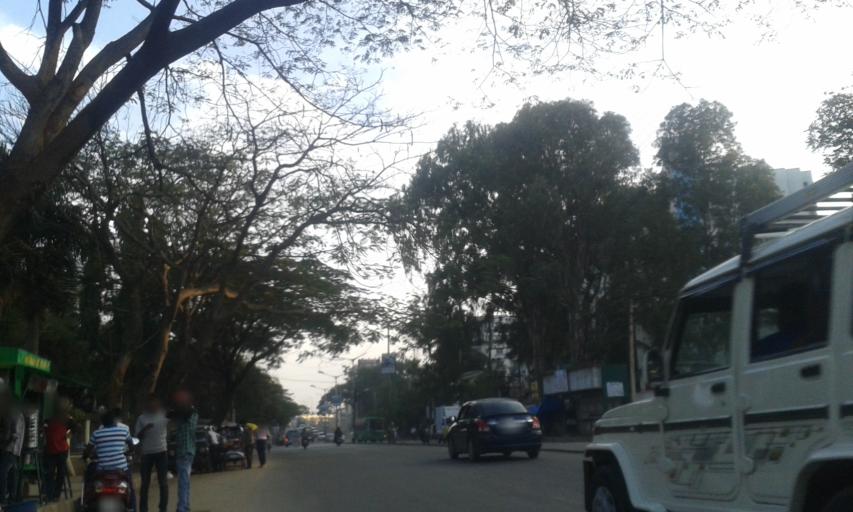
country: IN
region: Karnataka
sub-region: Bangalore Rural
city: Hoskote
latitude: 13.0017
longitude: 77.7576
